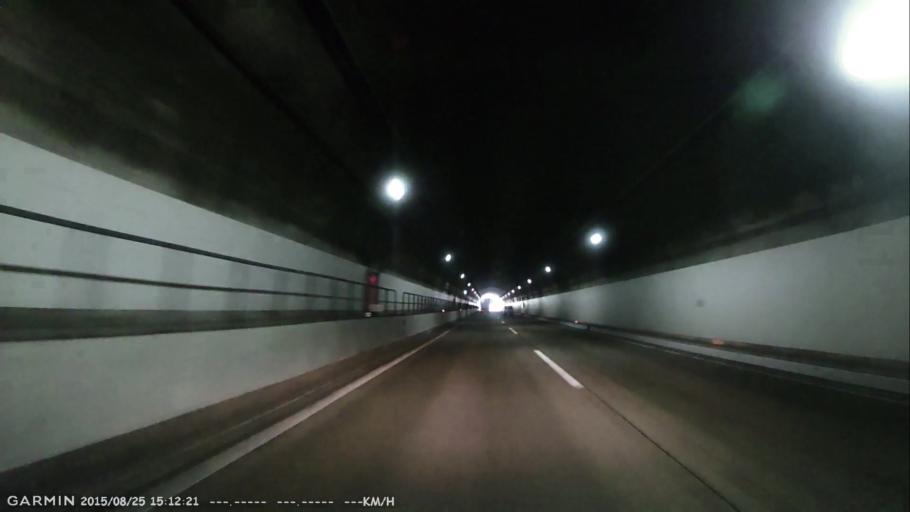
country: JP
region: Fukushima
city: Motomiya
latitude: 37.5007
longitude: 140.2580
